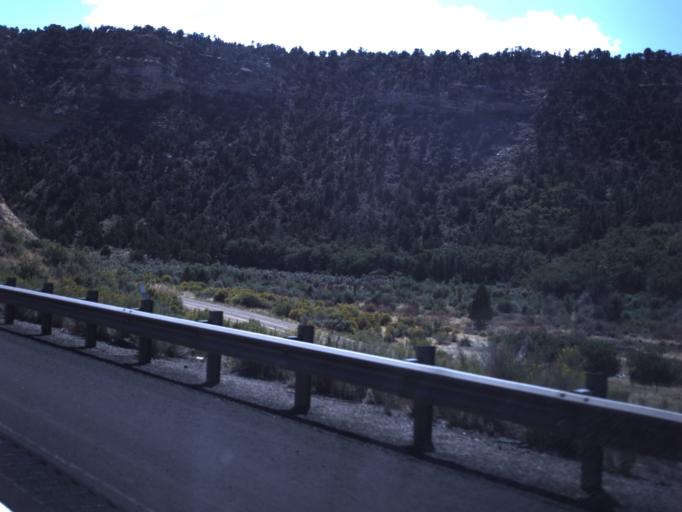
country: US
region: Utah
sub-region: Sevier County
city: Salina
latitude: 38.9102
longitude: -111.7104
